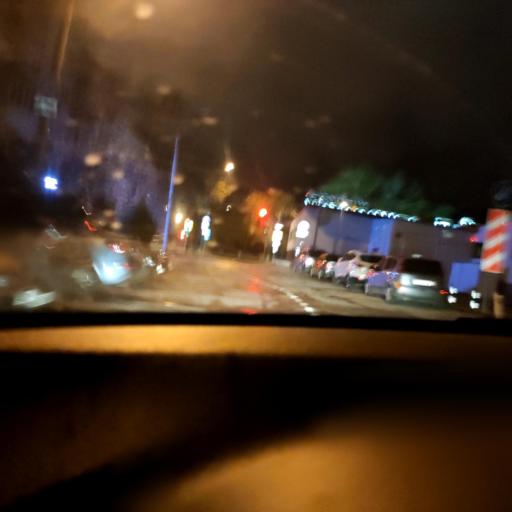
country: RU
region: Samara
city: Samara
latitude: 53.1977
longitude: 50.1607
